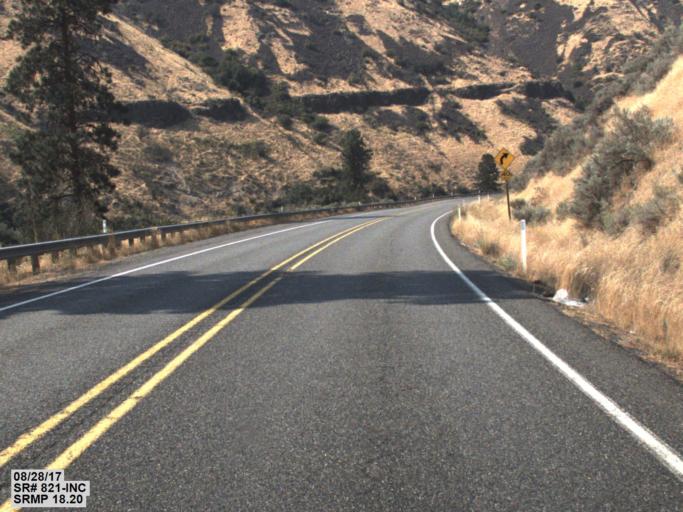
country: US
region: Washington
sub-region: Kittitas County
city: Kittitas
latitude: 46.8751
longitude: -120.4935
